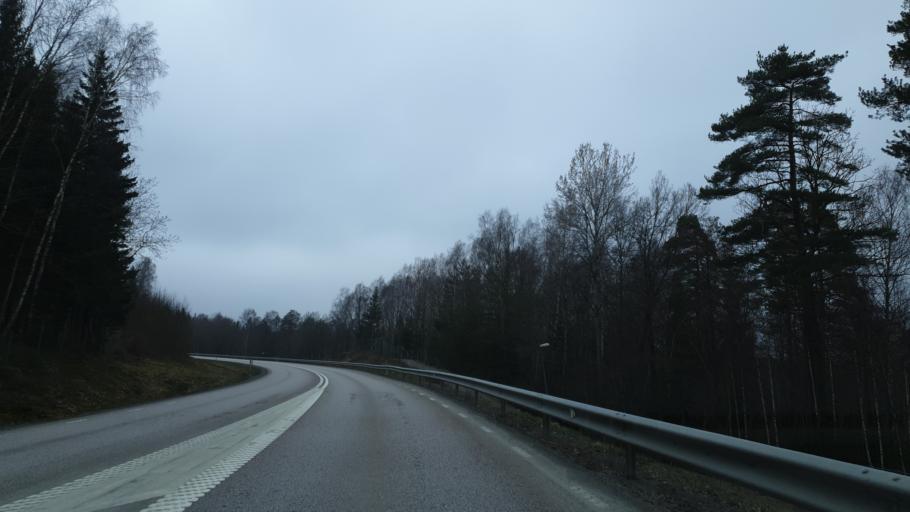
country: SE
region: Vaestra Goetaland
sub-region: Harryda Kommun
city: Ravlanda
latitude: 57.6206
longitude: 12.4326
